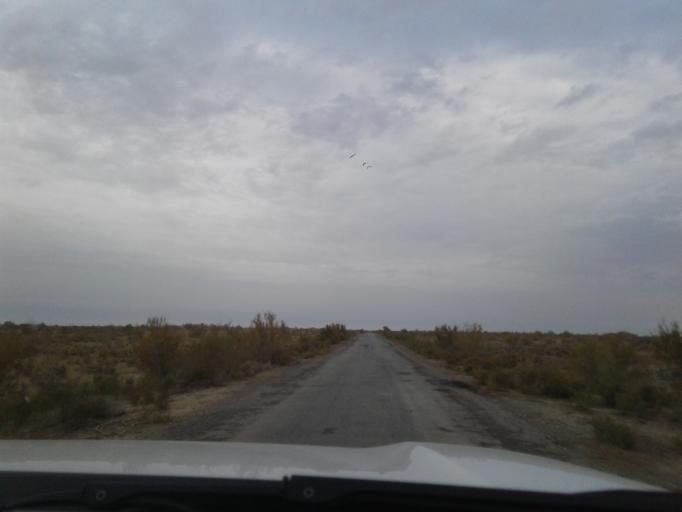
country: TM
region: Mary
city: Mary
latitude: 38.4663
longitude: 61.6701
